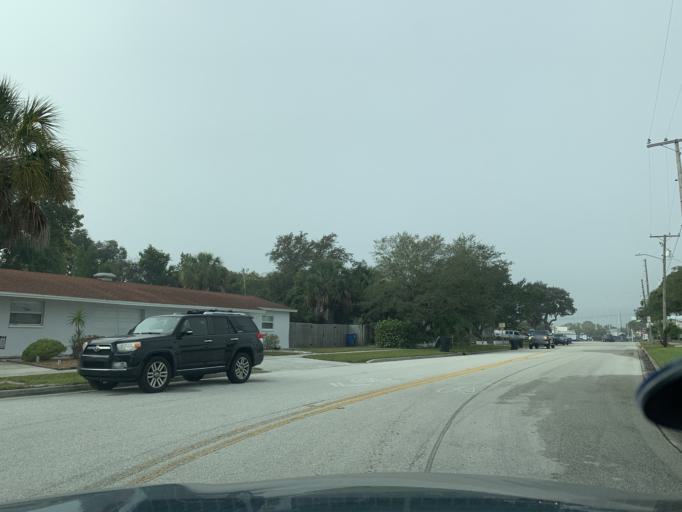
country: US
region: Florida
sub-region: Pinellas County
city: Saint Petersburg
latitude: 27.7559
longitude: -82.6310
